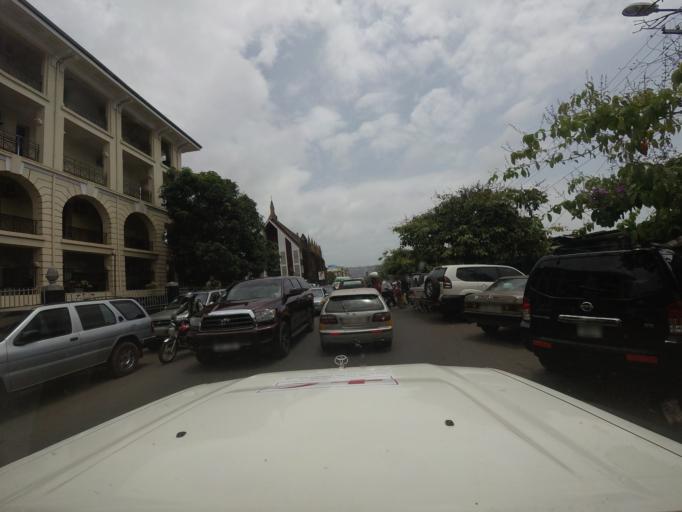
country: SL
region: Western Area
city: Freetown
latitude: 8.4891
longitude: -13.2359
